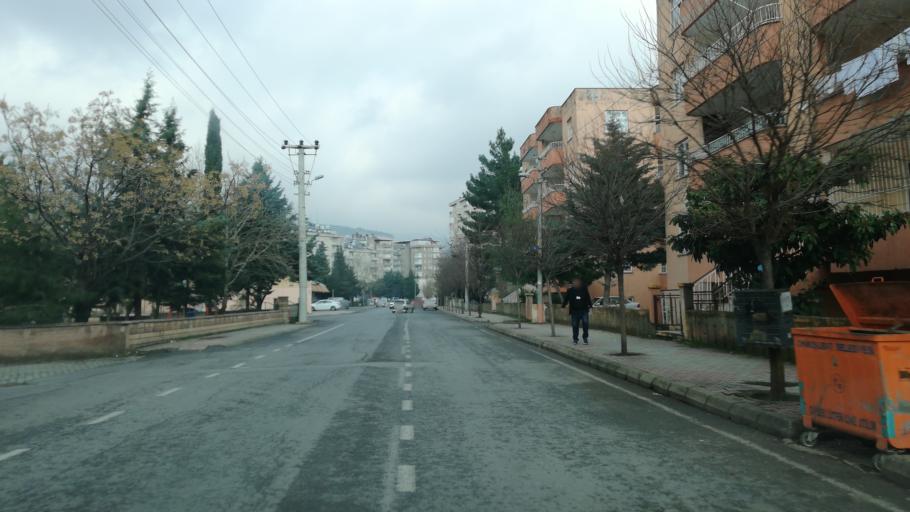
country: TR
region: Kahramanmaras
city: Kahramanmaras
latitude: 37.5838
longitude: 36.9005
